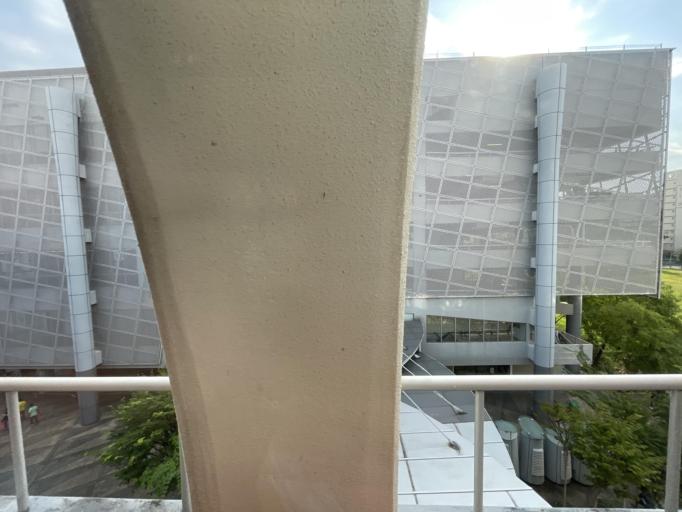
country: SG
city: Singapore
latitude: 1.3432
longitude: 103.9533
